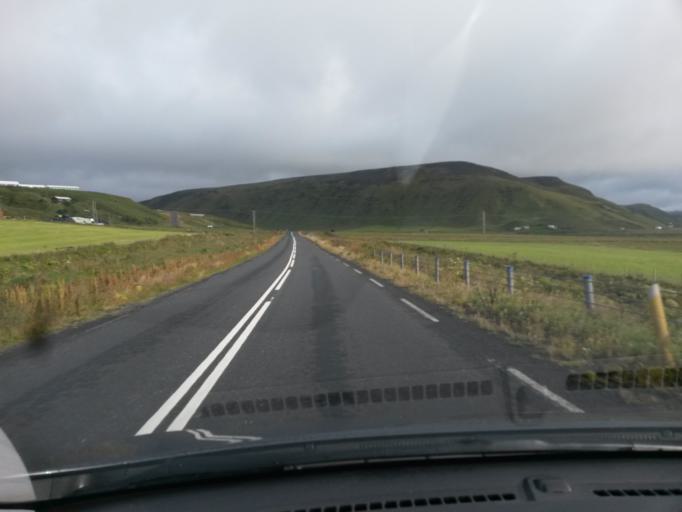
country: IS
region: South
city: Vestmannaeyjar
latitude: 63.4424
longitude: -19.1431
